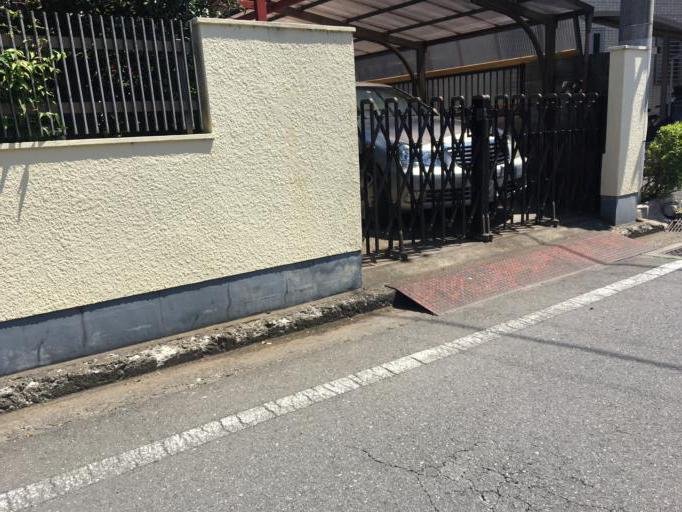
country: JP
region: Saitama
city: Kawagoe
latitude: 35.9276
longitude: 139.4450
